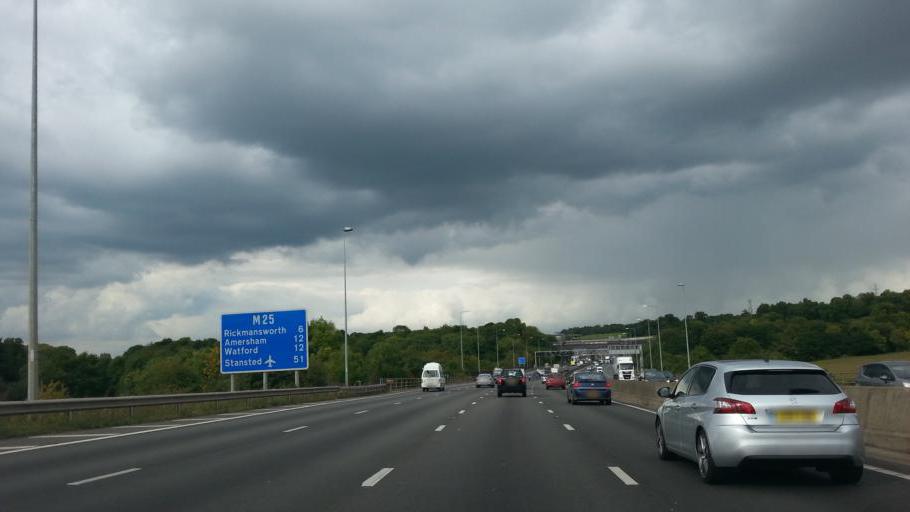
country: GB
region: England
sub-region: Buckinghamshire
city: Gerrards Cross
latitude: 51.5779
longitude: -0.5359
